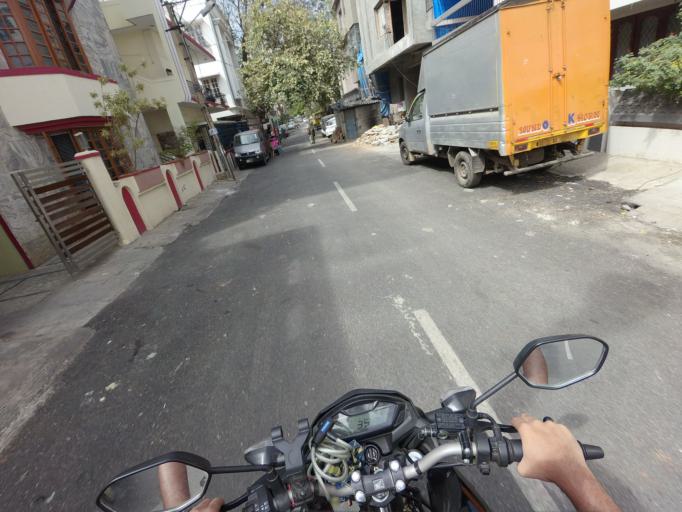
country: IN
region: Karnataka
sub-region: Bangalore Urban
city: Bangalore
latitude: 12.9724
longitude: 77.5414
